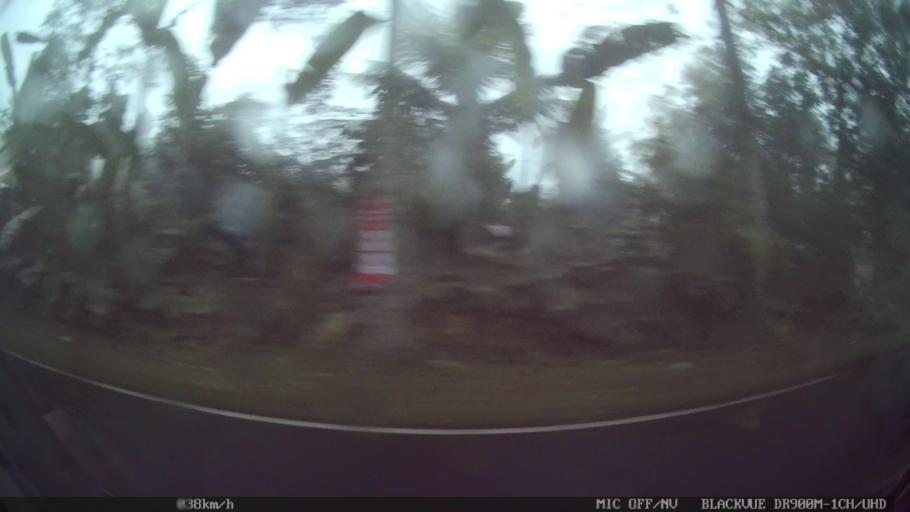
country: ID
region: Bali
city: Banjar Taro Kelod
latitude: -8.3318
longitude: 115.2866
